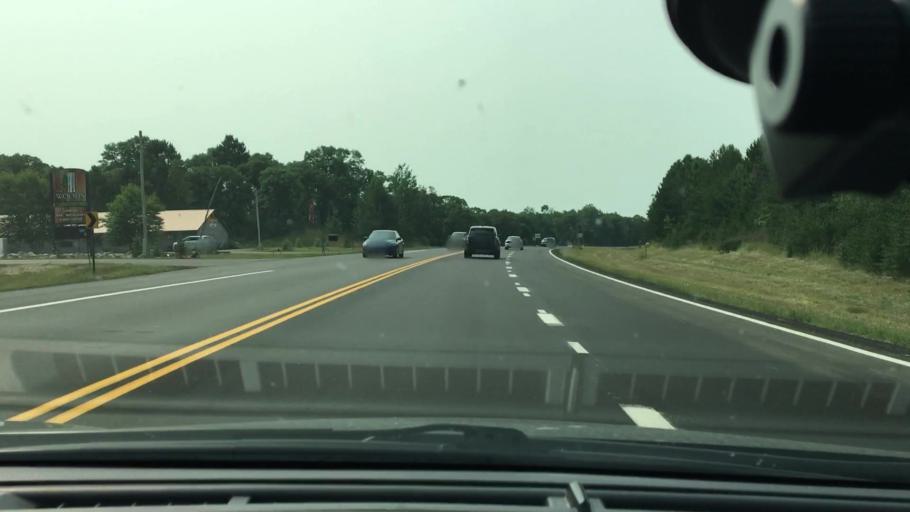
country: US
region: Minnesota
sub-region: Crow Wing County
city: Brainerd
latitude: 46.4372
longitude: -94.1715
